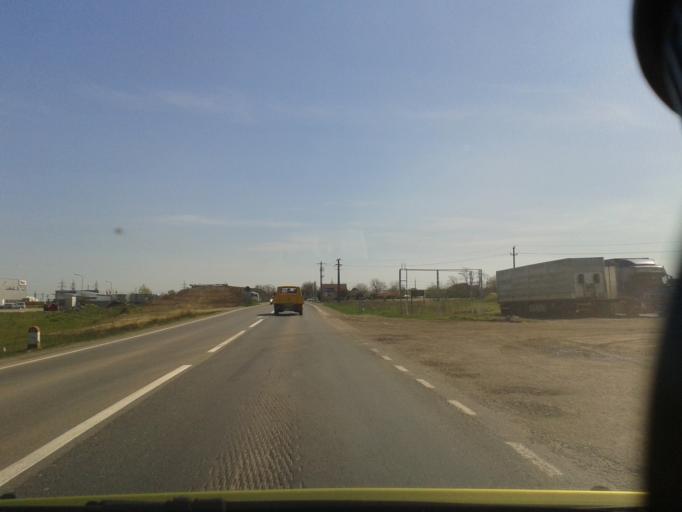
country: RO
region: Arad
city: Arad
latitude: 46.2159
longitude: 21.3172
